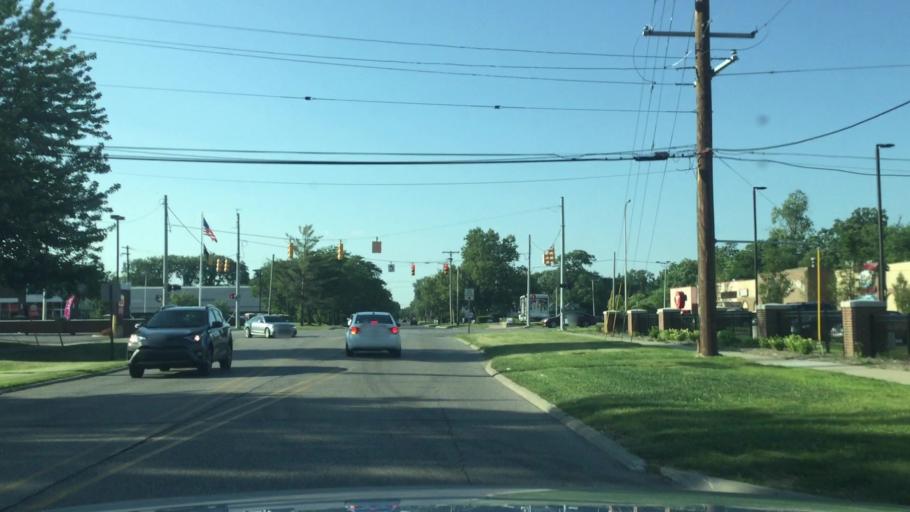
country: US
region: Michigan
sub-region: Wayne County
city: Westland
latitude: 42.3239
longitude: -83.3794
